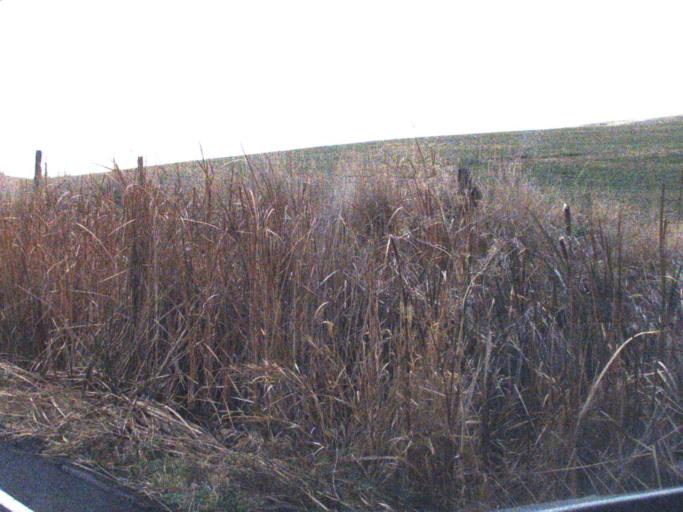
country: US
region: Washington
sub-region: Columbia County
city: Dayton
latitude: 46.5040
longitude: -118.0229
